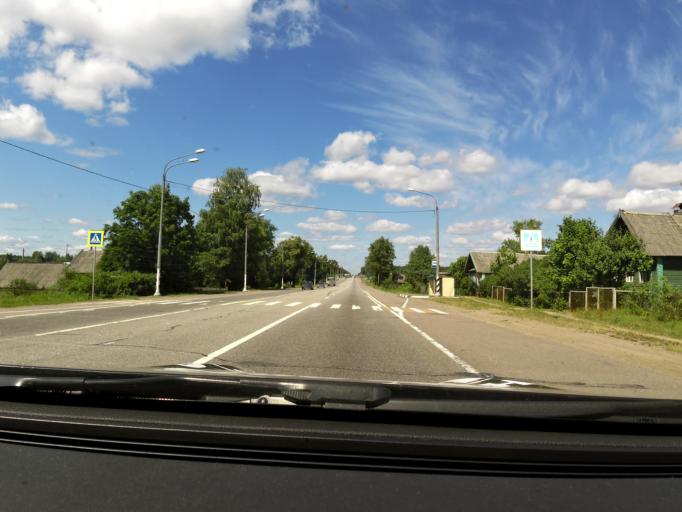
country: RU
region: Tverskaya
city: Kuzhenkino
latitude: 57.8109
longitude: 33.8445
